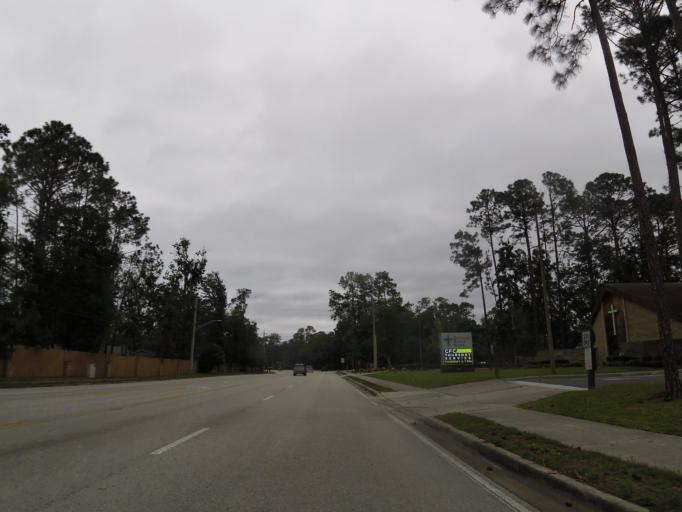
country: US
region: Florida
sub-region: Saint Johns County
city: Fruit Cove
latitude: 30.1879
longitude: -81.6079
